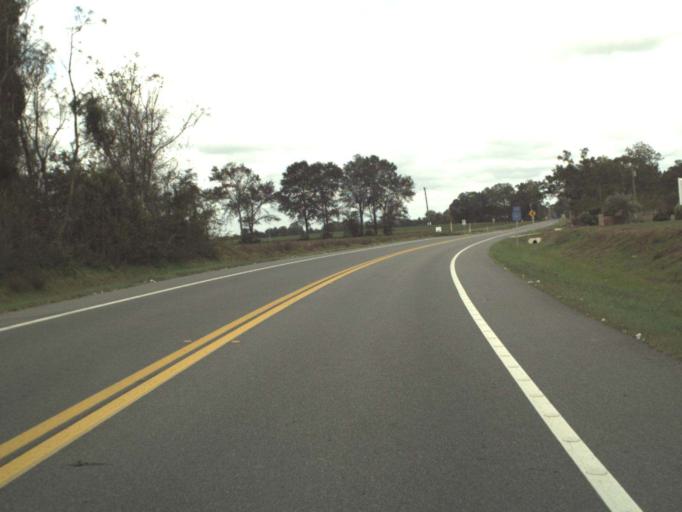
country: US
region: Florida
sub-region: Escambia County
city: Century
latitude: 30.9124
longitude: -87.1680
